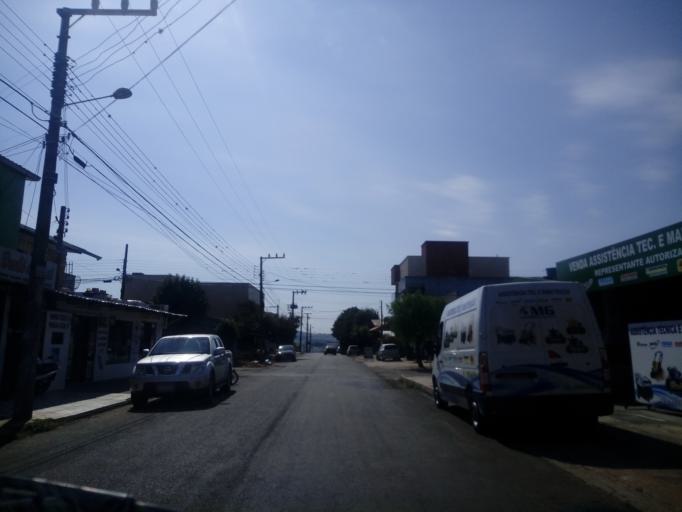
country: BR
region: Santa Catarina
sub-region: Chapeco
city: Chapeco
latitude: -27.0860
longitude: -52.6293
